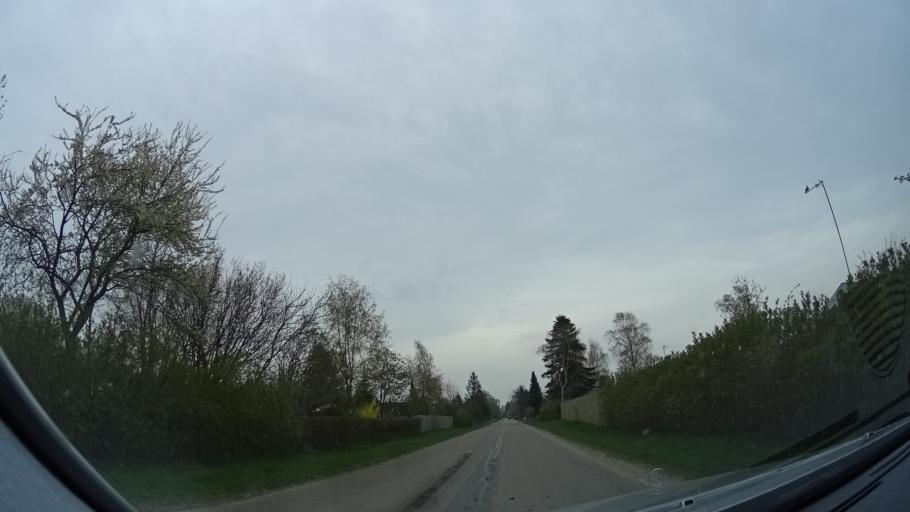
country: DK
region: Zealand
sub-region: Lejre Kommune
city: Ejby
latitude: 55.7066
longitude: 11.8532
